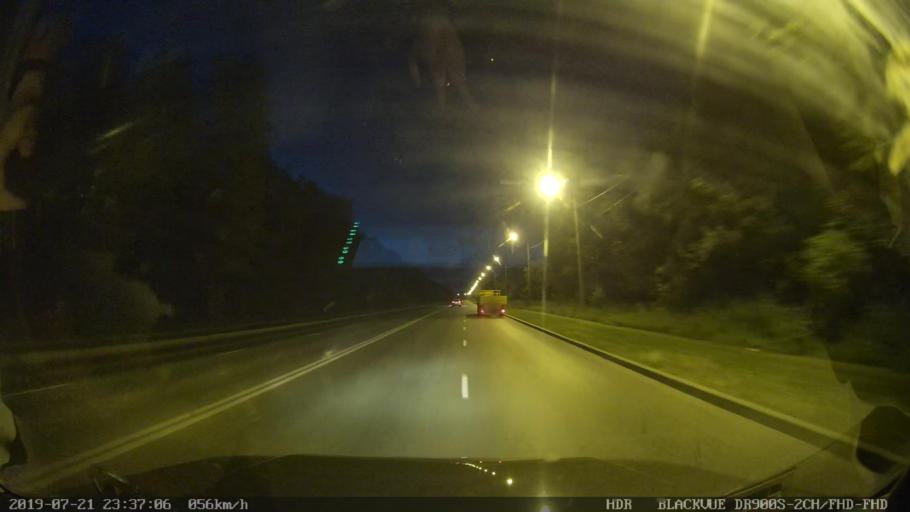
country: RU
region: Perm
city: Kondratovo
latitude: 57.9447
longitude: 56.1724
